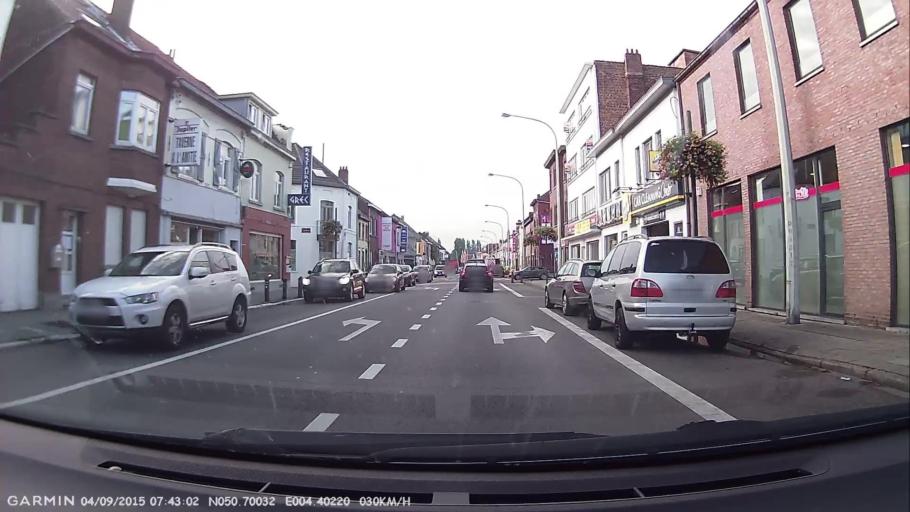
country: BE
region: Wallonia
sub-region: Province du Brabant Wallon
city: Waterloo
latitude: 50.7001
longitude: 4.4022
